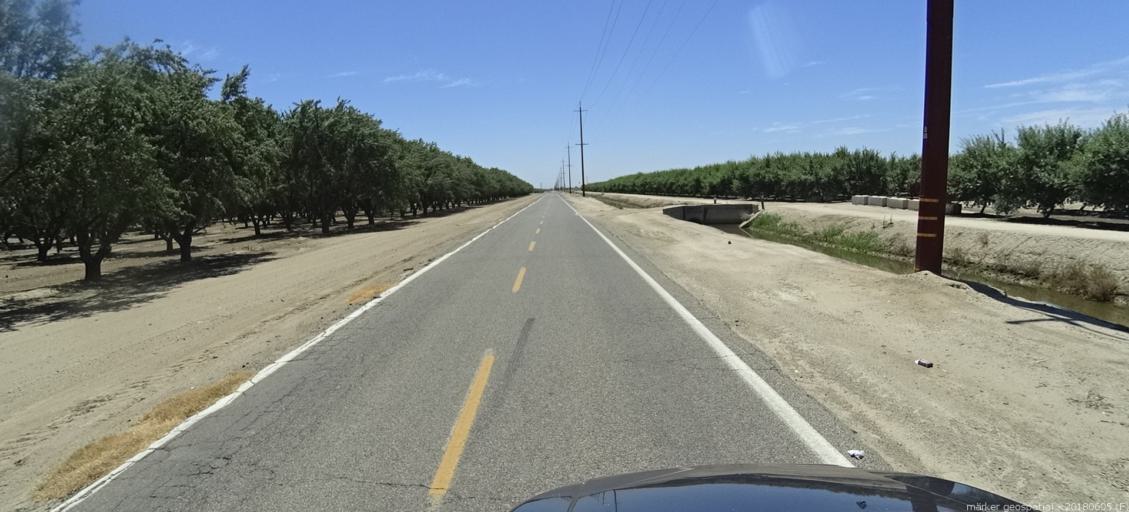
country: US
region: California
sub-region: Madera County
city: Chowchilla
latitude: 37.1168
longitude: -120.3109
